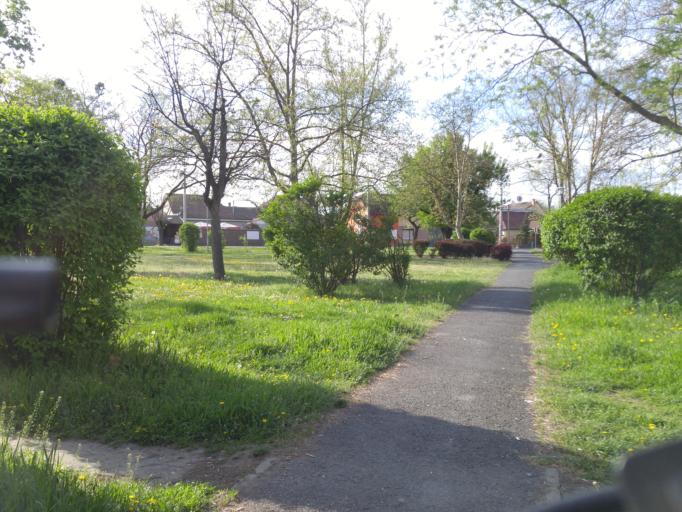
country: HU
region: Budapest
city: Budapest XX. keruelet
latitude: 47.4333
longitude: 19.1271
